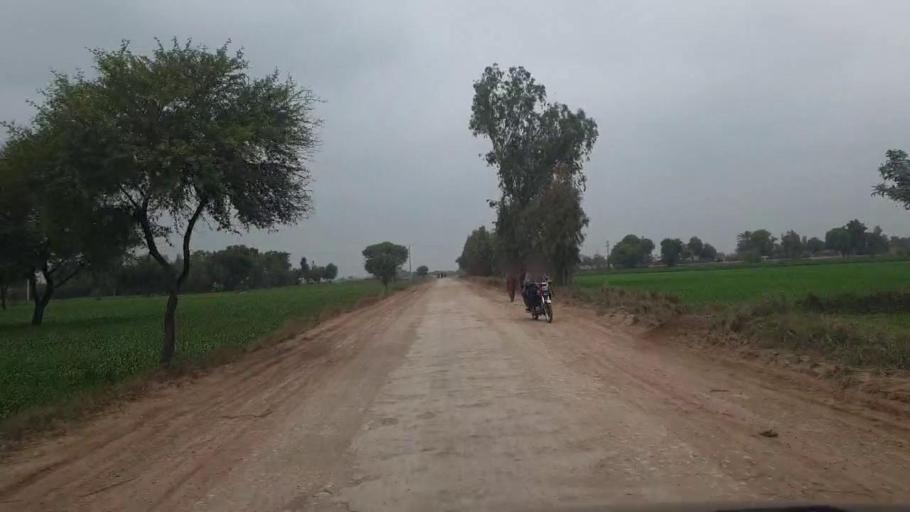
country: PK
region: Sindh
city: Shahdadpur
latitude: 25.9434
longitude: 68.7249
